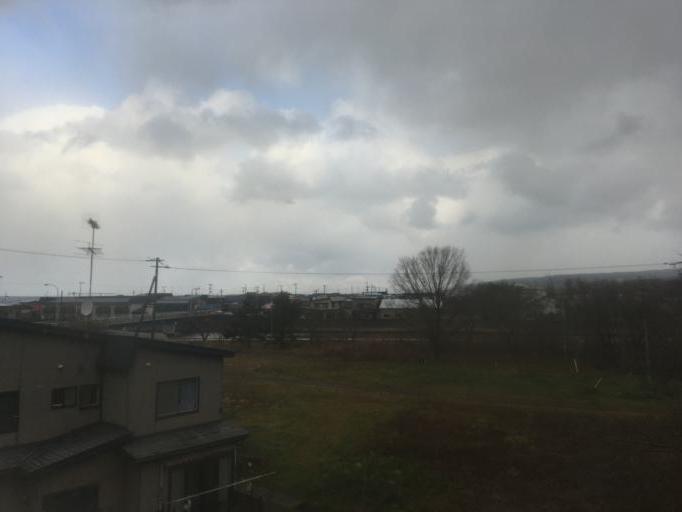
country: JP
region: Aomori
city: Goshogawara
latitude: 41.1821
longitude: 140.4876
